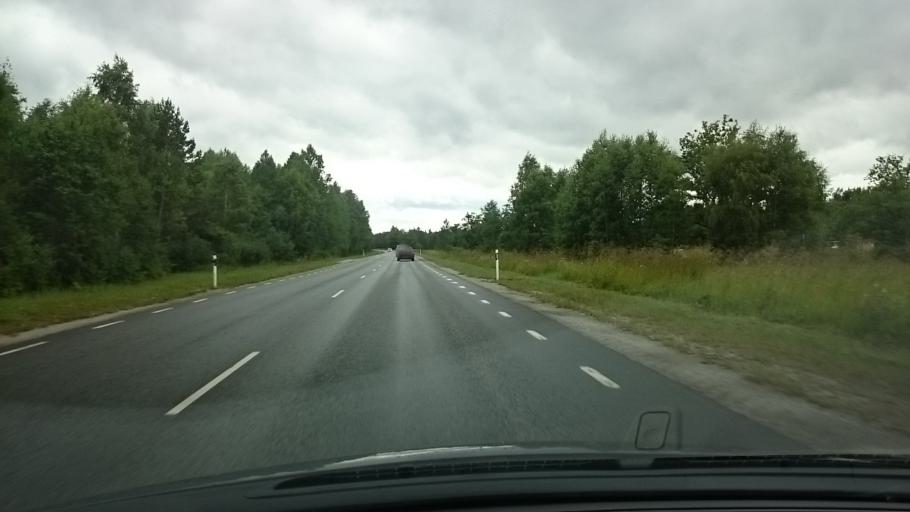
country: EE
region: Harju
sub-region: Keila linn
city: Keila
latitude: 59.2767
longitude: 24.3017
